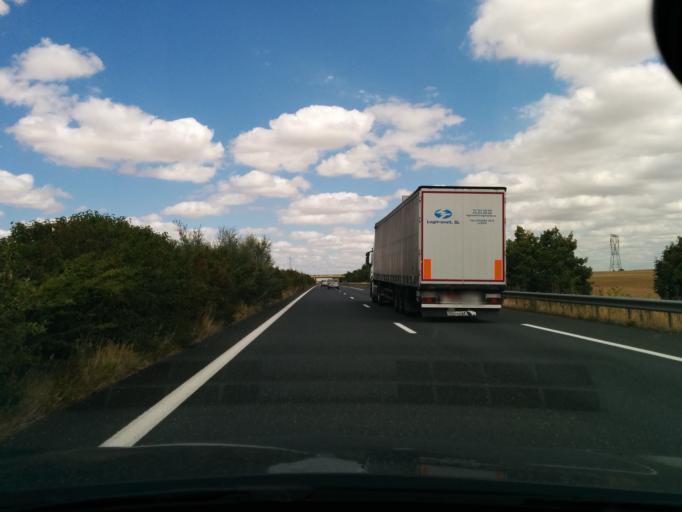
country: FR
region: Centre
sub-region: Departement de l'Indre
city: Saint-Maur
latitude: 46.8285
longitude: 1.6441
